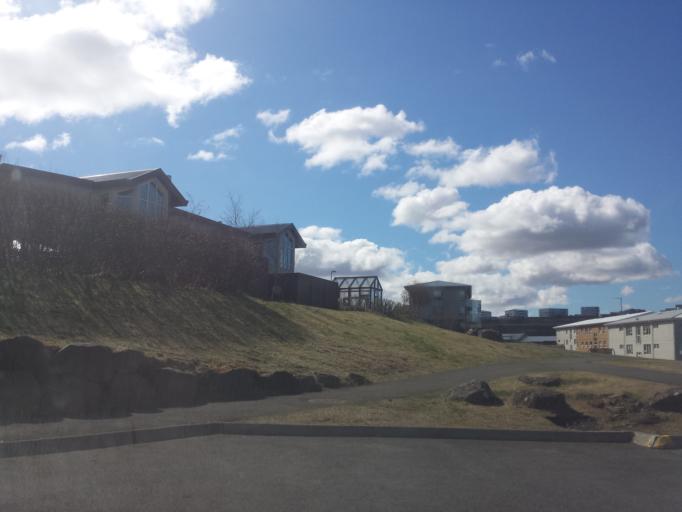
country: IS
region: Capital Region
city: Reykjavik
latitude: 64.0926
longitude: -21.8519
